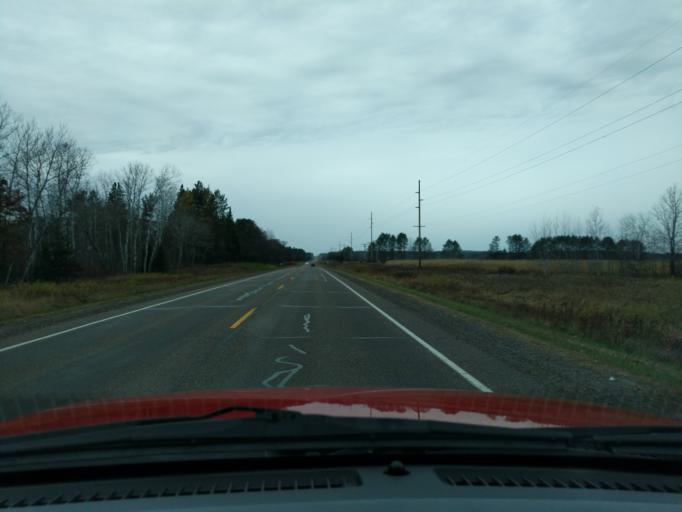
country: US
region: Wisconsin
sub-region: Washburn County
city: Shell Lake
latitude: 45.8151
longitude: -91.9887
